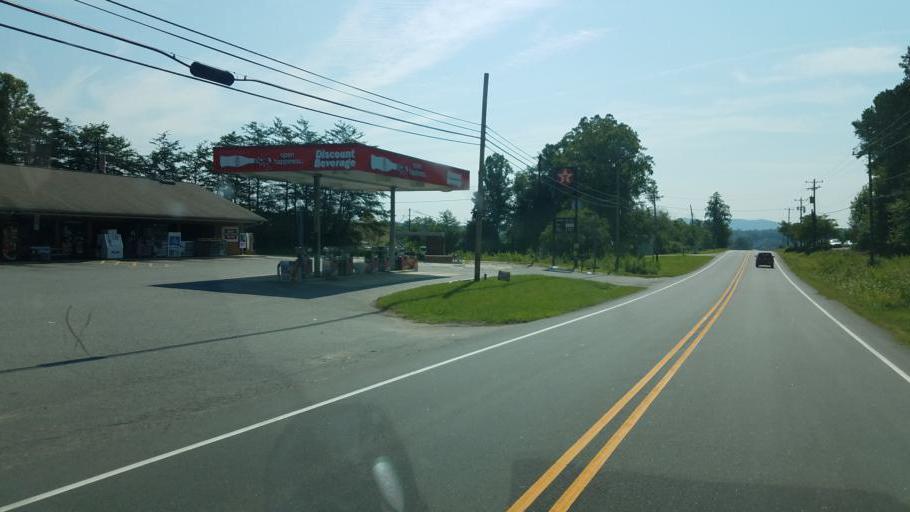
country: US
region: North Carolina
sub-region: Burke County
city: Morganton
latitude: 35.7563
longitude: -81.7237
